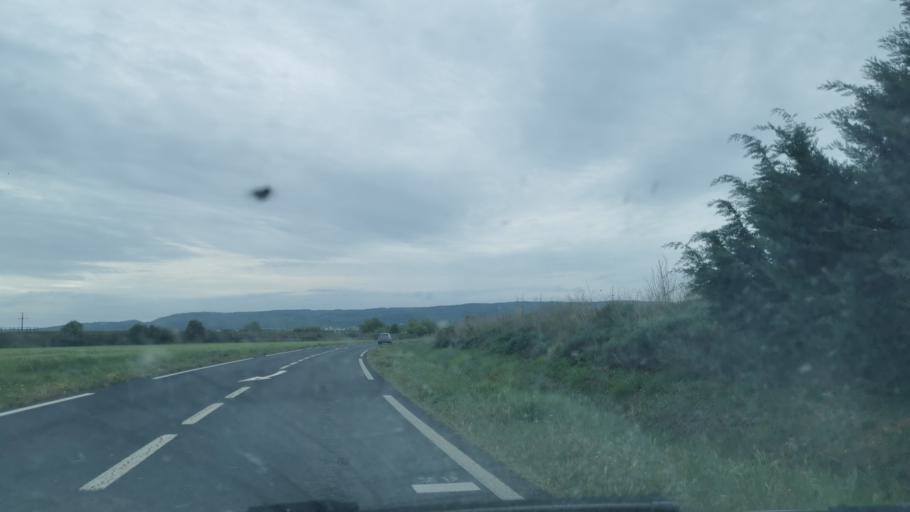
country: FR
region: Languedoc-Roussillon
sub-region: Departement de l'Herault
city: Montbazin
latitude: 43.5131
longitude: 3.6801
